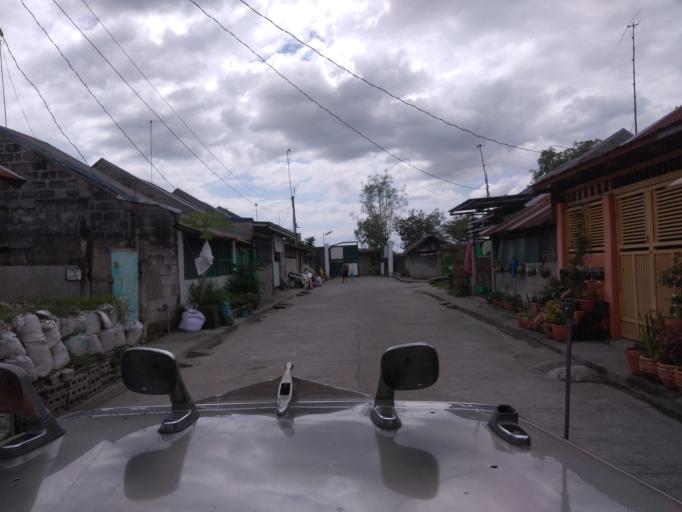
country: PH
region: Central Luzon
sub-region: Province of Pampanga
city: Pandacaqui
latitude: 15.1762
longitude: 120.6627
